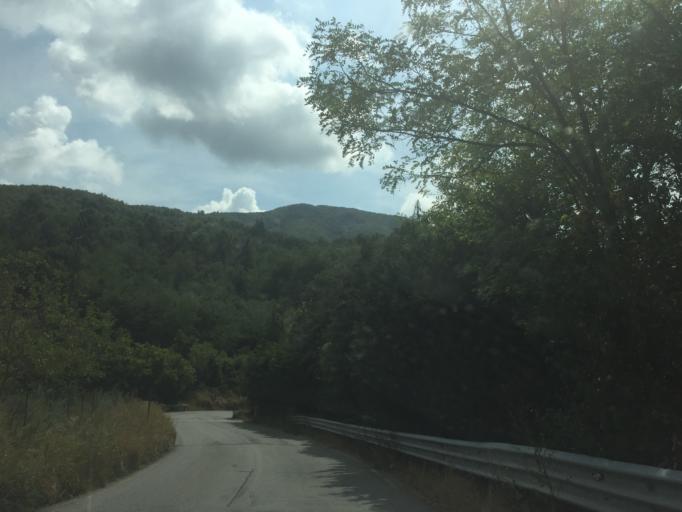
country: IT
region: Tuscany
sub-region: Provincia di Pistoia
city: Campo Tizzoro
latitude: 44.0428
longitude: 10.8315
